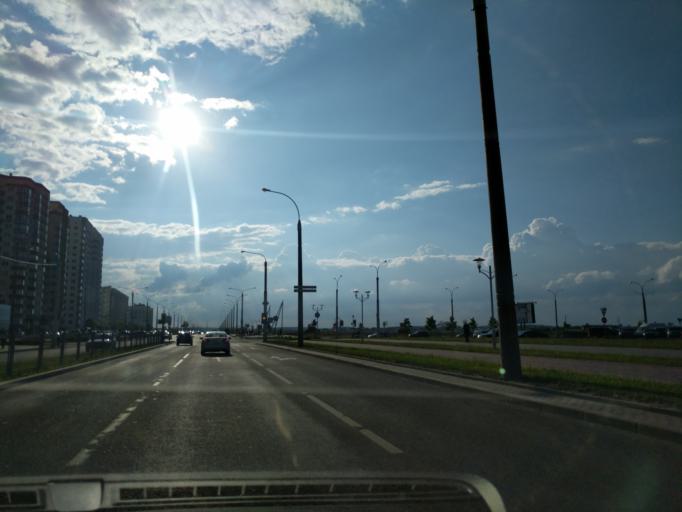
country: BY
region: Minsk
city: Zhdanovichy
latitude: 53.9165
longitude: 27.4290
